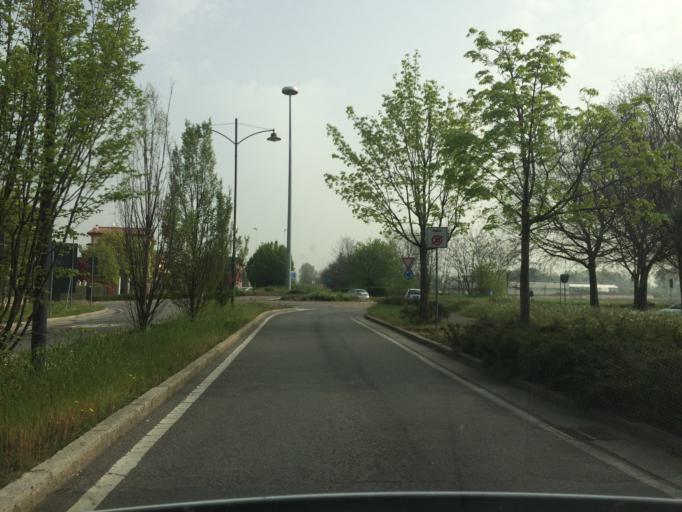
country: IT
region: Lombardy
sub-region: Provincia di Brescia
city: Flero
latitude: 45.5036
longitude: 10.1727
